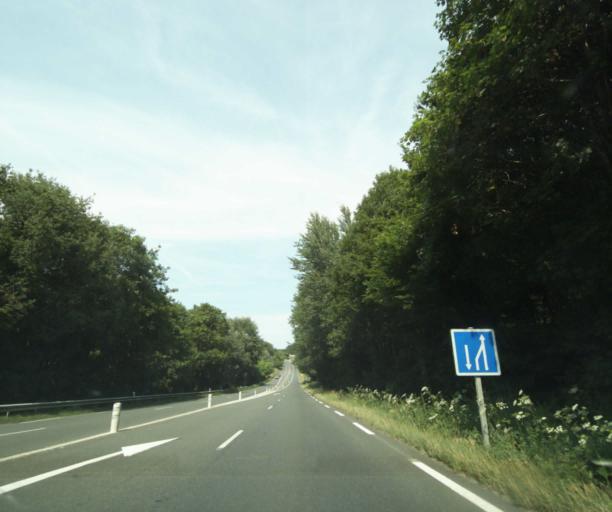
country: FR
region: Centre
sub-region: Departement d'Indre-et-Loire
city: Sainte-Maure-de-Touraine
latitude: 47.1403
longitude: 0.6419
